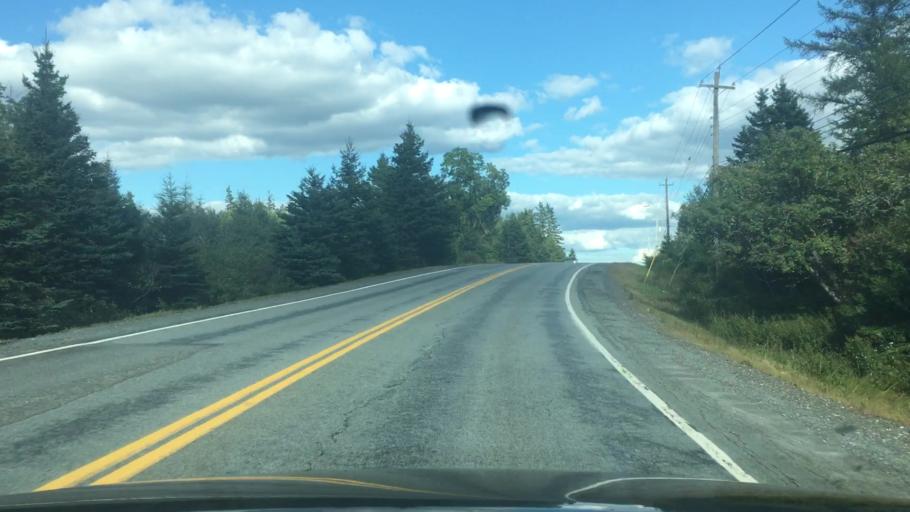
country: CA
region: Nova Scotia
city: Halifax
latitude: 44.5971
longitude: -63.6928
